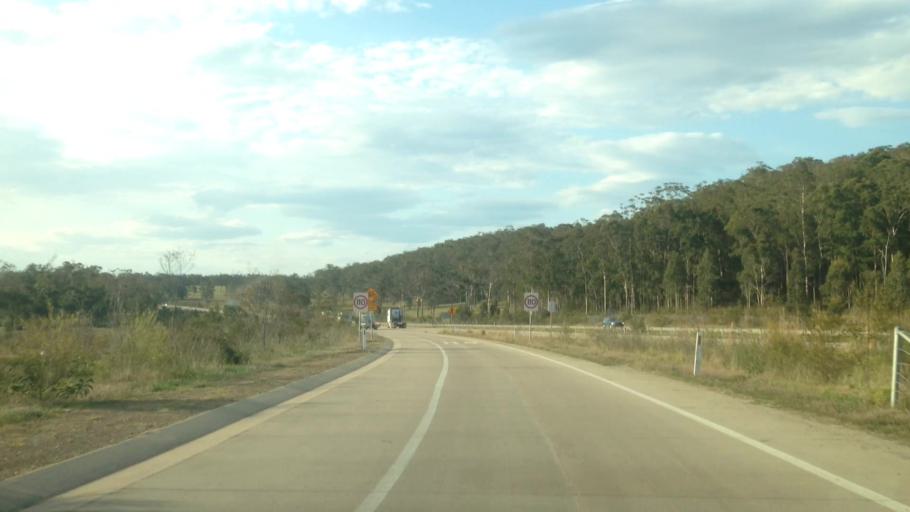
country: AU
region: New South Wales
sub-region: Cessnock
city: Heddon Greta
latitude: -32.8432
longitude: 151.5422
